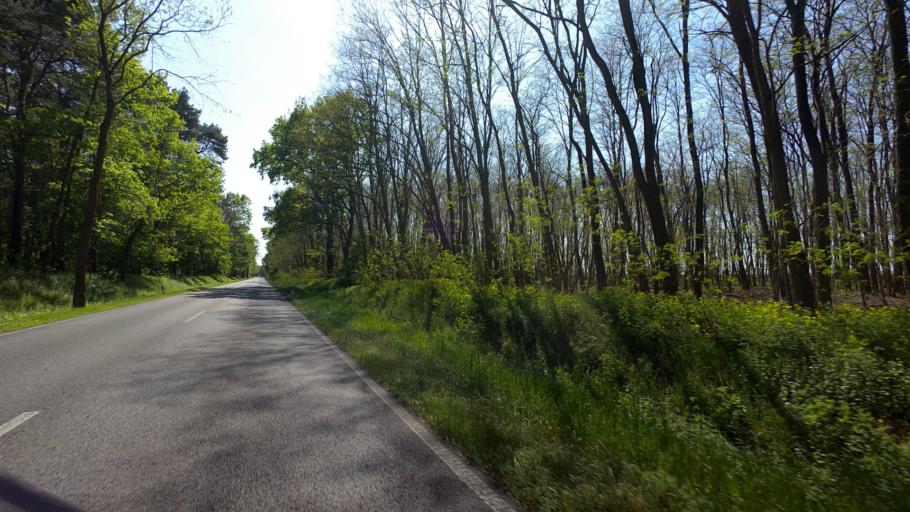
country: DE
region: Brandenburg
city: Tauche
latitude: 52.1257
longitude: 14.1960
